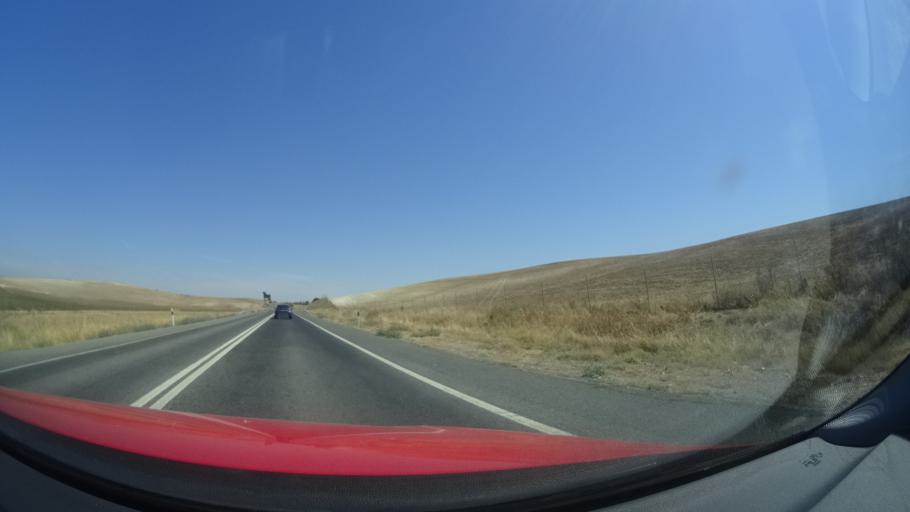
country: ES
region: Andalusia
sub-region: Provincia de Sevilla
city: Las Cabezas de San Juan
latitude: 36.9632
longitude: -5.8836
